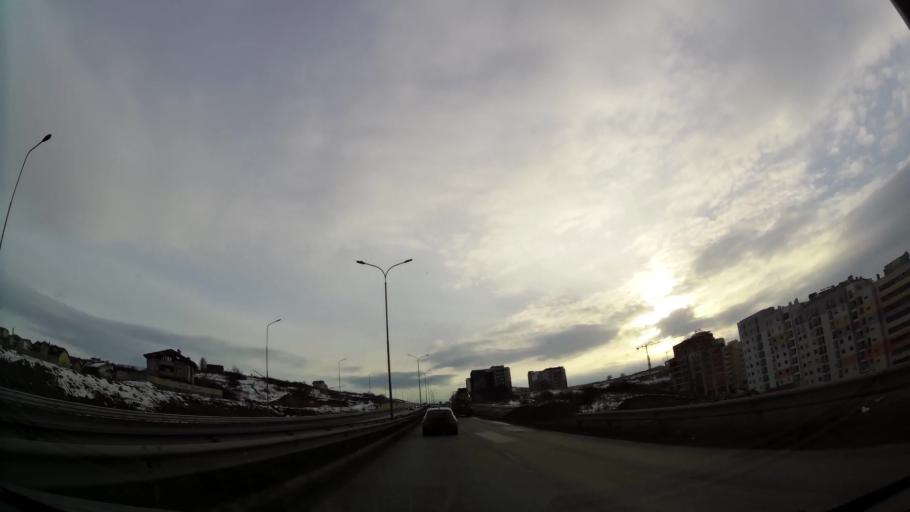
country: XK
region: Pristina
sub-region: Komuna e Prishtines
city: Pristina
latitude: 42.6405
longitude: 21.1550
